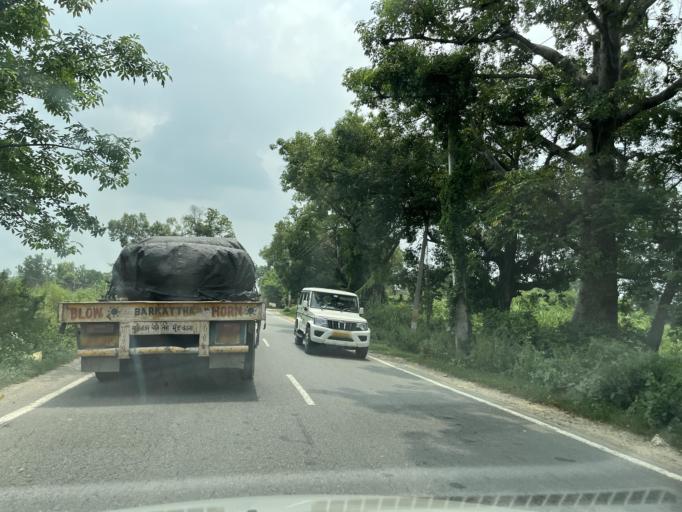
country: IN
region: Uttar Pradesh
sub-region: Bijnor
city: Najibabad
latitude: 29.5823
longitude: 78.3385
